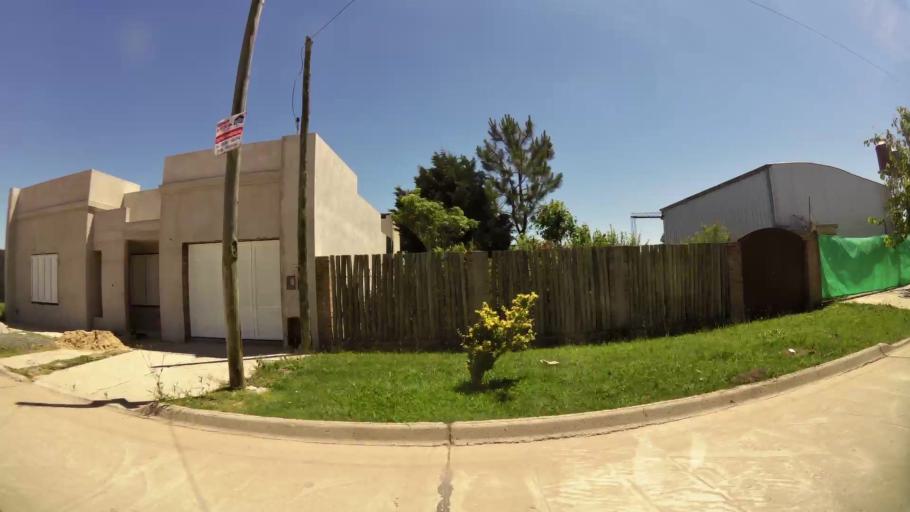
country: AR
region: Santa Fe
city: Esperanza
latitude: -31.3957
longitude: -61.0859
